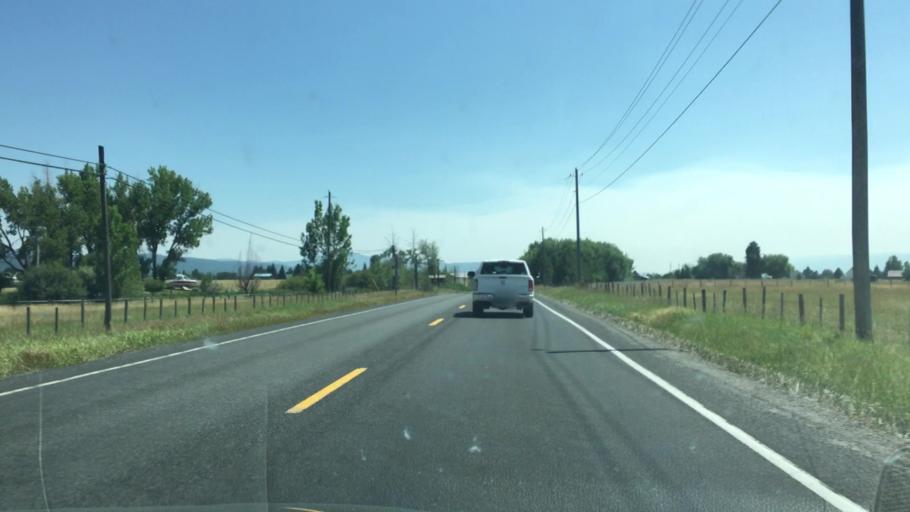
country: US
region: Idaho
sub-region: Valley County
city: McCall
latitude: 44.8451
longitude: -116.0889
